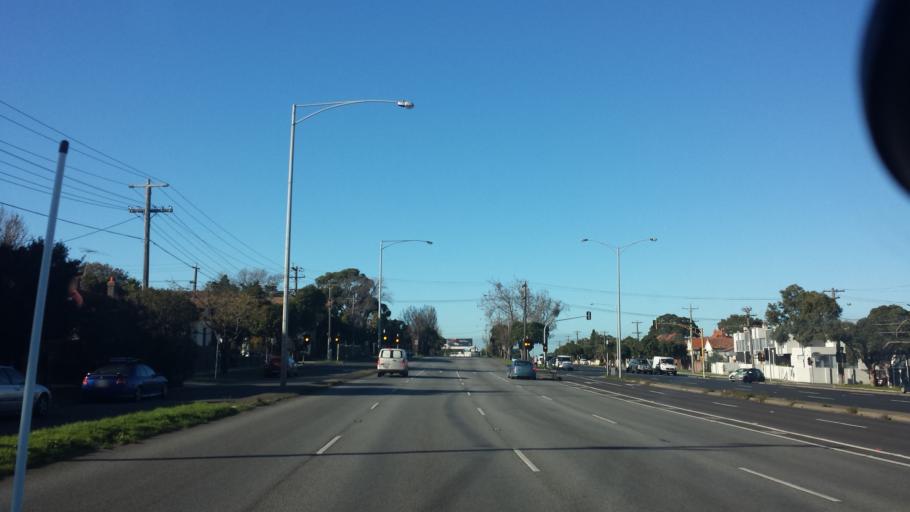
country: AU
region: Victoria
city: Ripponlea
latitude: -37.8855
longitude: 144.9986
